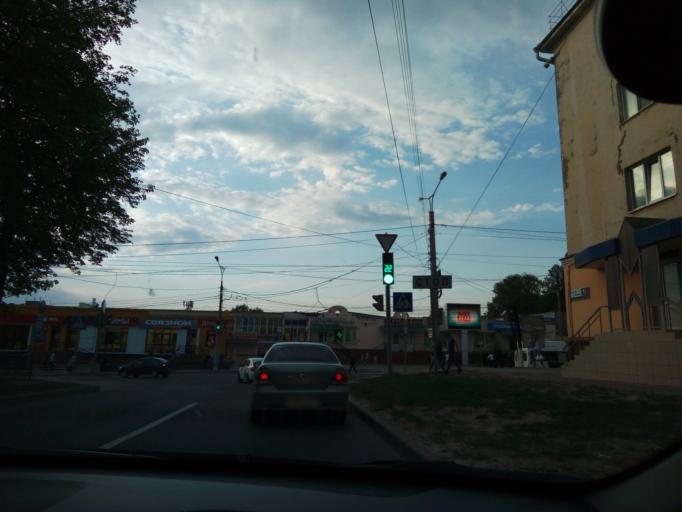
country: RU
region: Chuvashia
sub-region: Cheboksarskiy Rayon
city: Cheboksary
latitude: 56.1223
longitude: 47.2503
